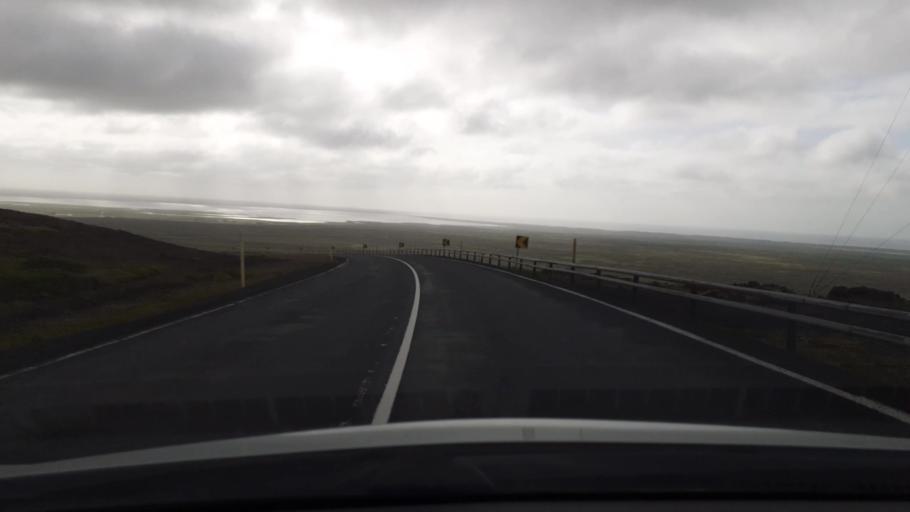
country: IS
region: South
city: THorlakshoefn
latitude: 63.9312
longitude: -21.3922
